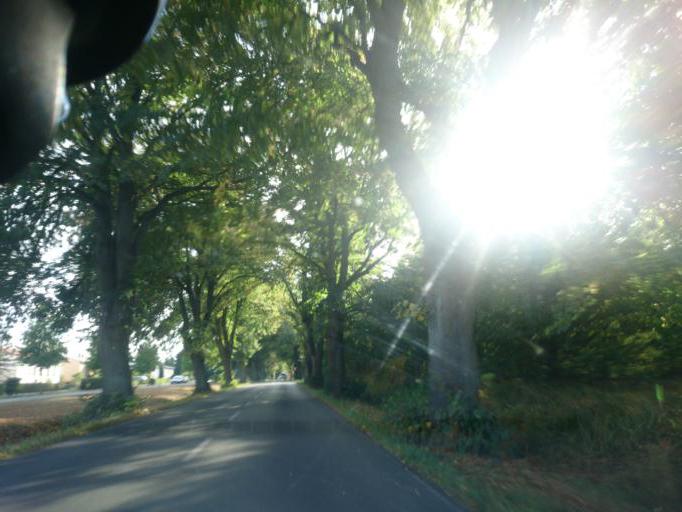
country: DE
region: Mecklenburg-Vorpommern
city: Bad Doberan
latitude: 54.1130
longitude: 11.9107
